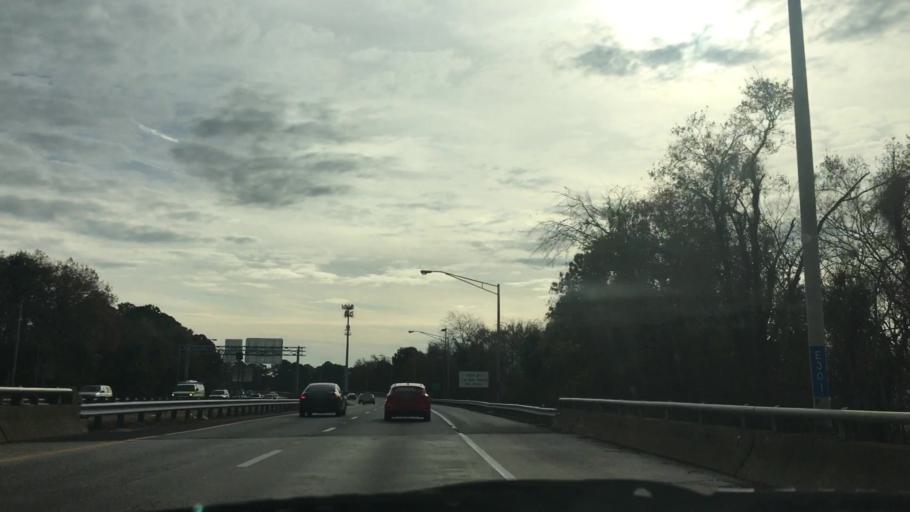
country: US
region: Virginia
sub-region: City of Norfolk
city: Norfolk
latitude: 36.9467
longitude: -76.2665
